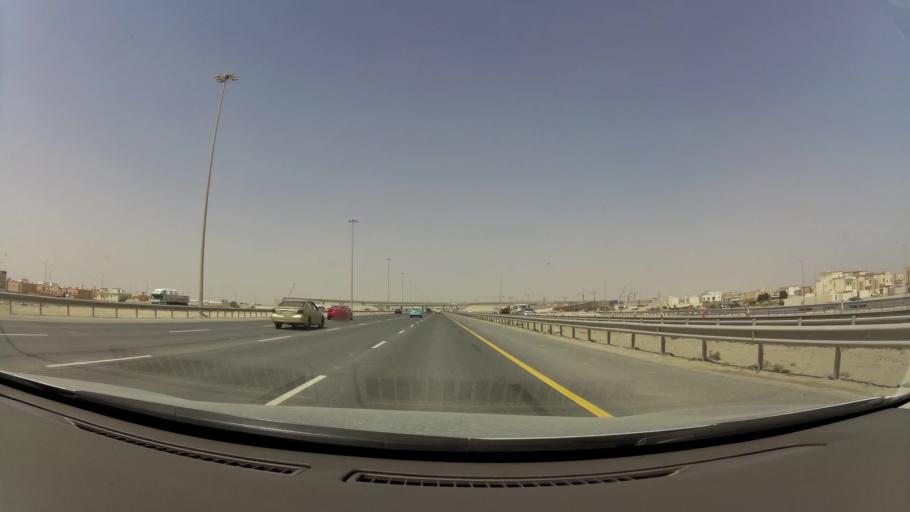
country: QA
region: Baladiyat Umm Salal
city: Umm Salal Muhammad
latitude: 25.3959
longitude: 51.4324
